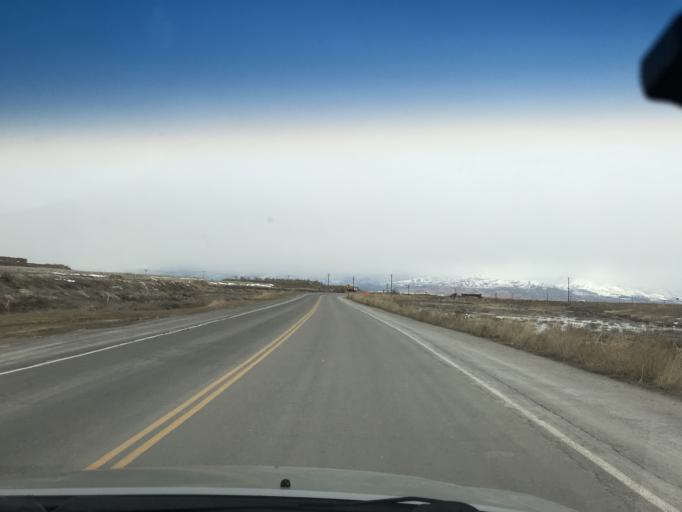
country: US
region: Utah
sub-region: Salt Lake County
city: Magna
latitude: 40.7723
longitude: -112.0668
